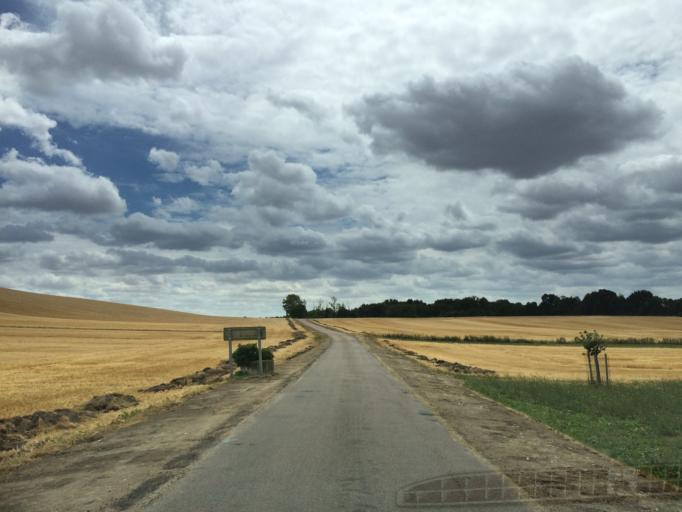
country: FR
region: Bourgogne
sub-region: Departement de l'Yonne
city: Fleury-la-Vallee
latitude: 47.8561
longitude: 3.4067
